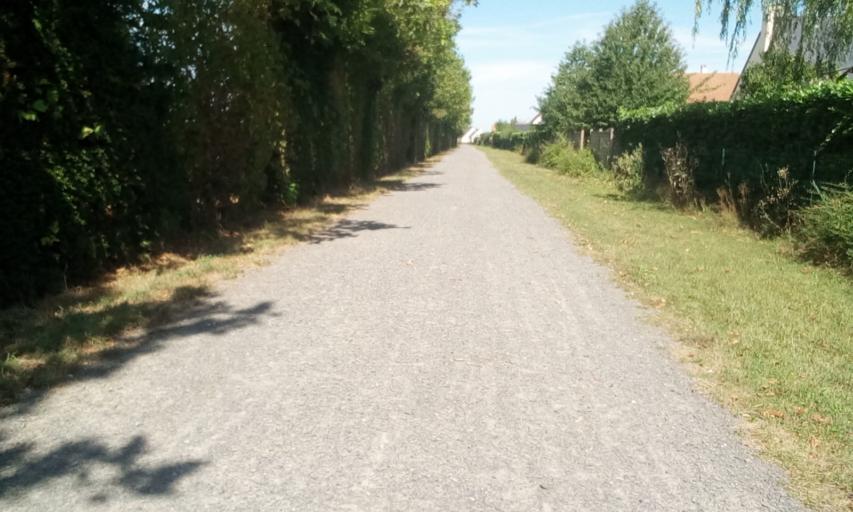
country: FR
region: Lower Normandy
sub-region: Departement du Calvados
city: Eterville
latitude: 49.1463
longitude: -0.4287
